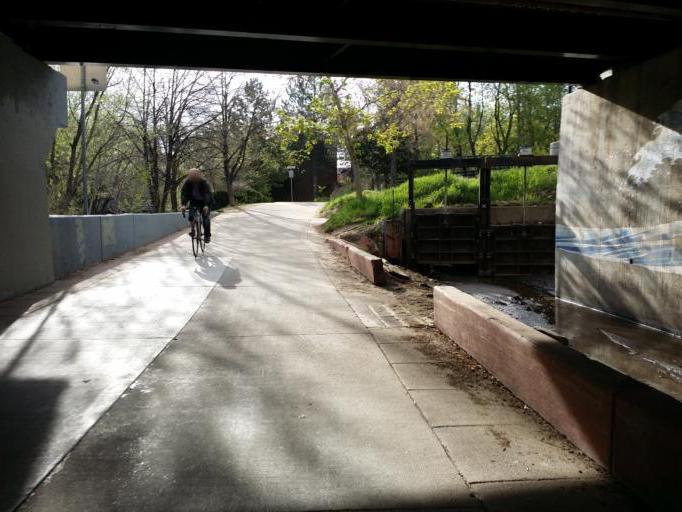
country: US
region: Colorado
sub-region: Boulder County
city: Boulder
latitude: 40.0112
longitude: -105.2588
